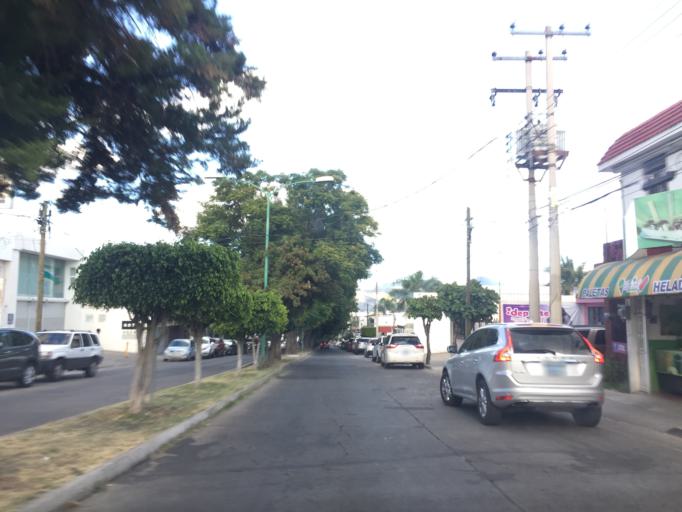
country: MX
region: Guanajuato
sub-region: Leon
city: La Ermita
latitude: 21.1500
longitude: -101.6994
